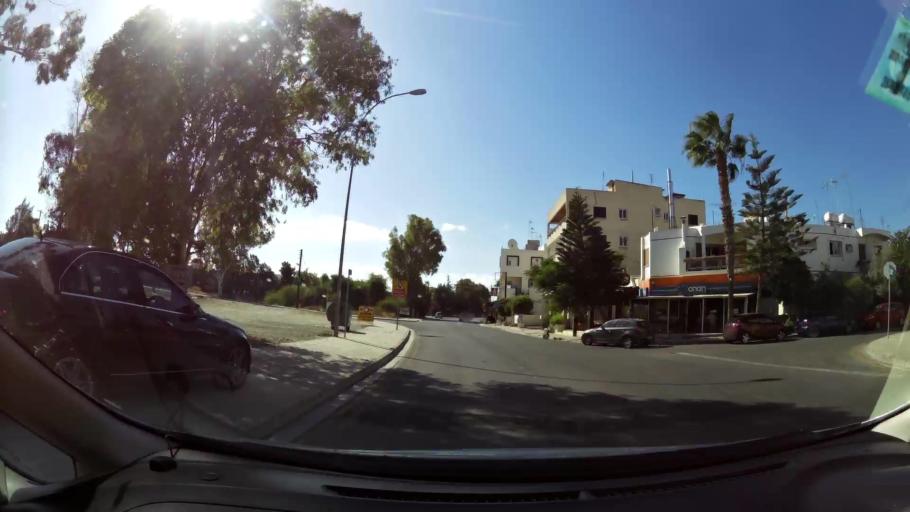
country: CY
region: Lefkosia
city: Nicosia
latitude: 35.1387
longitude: 33.3365
